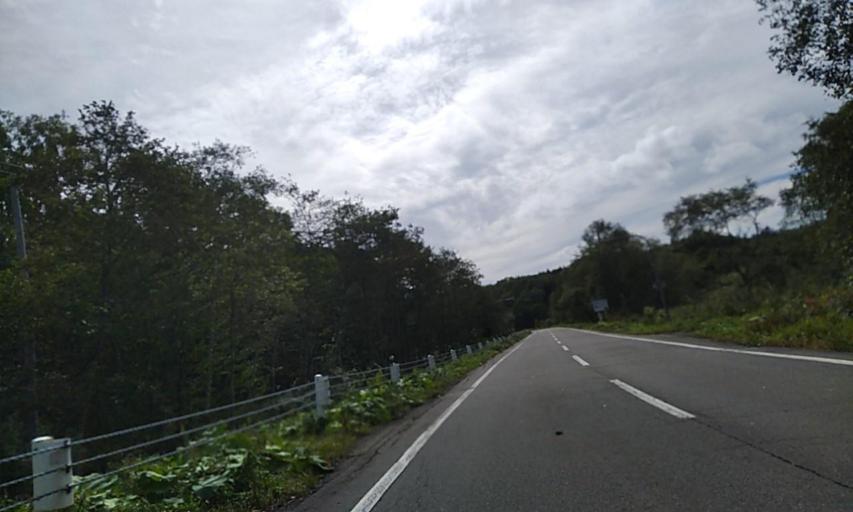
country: JP
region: Hokkaido
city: Kushiro
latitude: 42.8425
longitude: 143.8417
